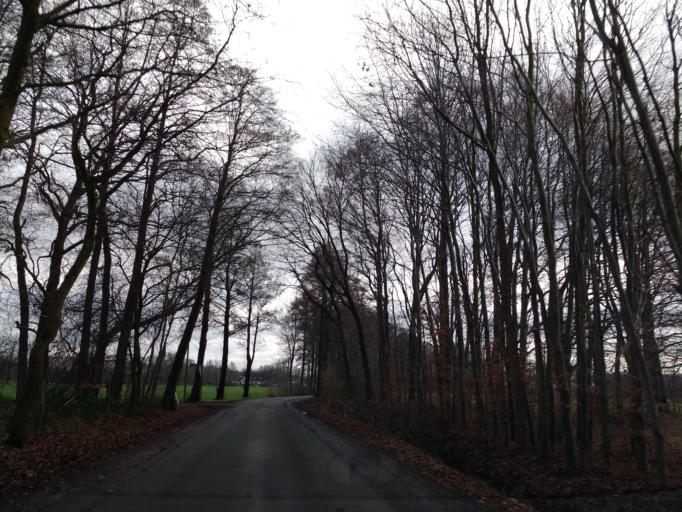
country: DE
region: North Rhine-Westphalia
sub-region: Regierungsbezirk Detmold
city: Hovelhof
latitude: 51.8245
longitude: 8.6905
